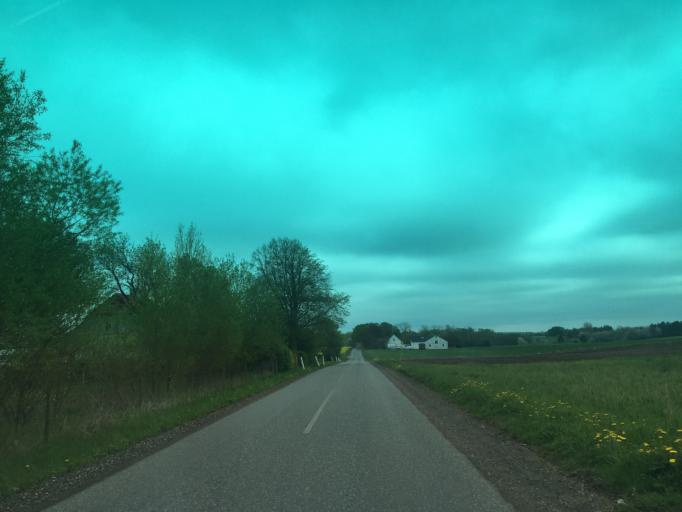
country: DK
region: Zealand
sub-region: Ringsted Kommune
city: Ringsted
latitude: 55.4185
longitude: 11.7083
